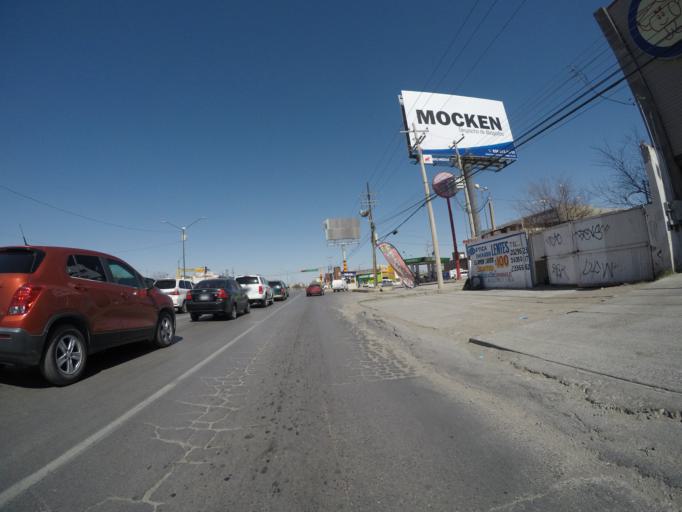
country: MX
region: Chihuahua
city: Ciudad Juarez
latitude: 31.7057
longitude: -106.4469
